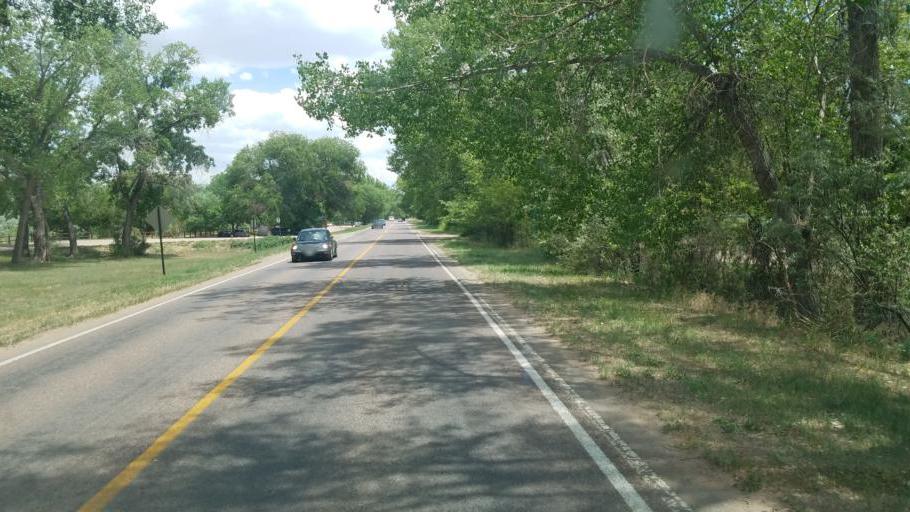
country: US
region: Colorado
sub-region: Fremont County
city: Lincoln Park
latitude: 38.4368
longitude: -105.2048
